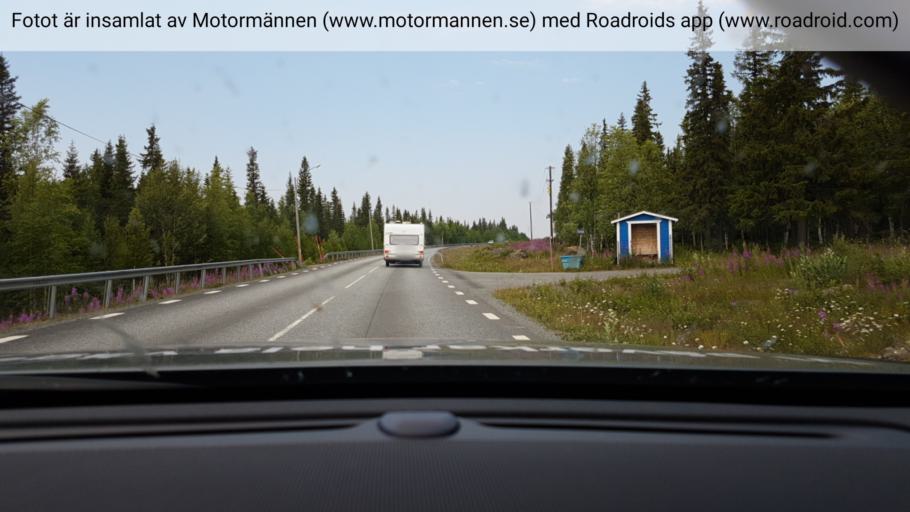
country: SE
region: Vaesterbotten
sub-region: Vilhelmina Kommun
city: Sjoberg
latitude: 65.4993
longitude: 15.6876
